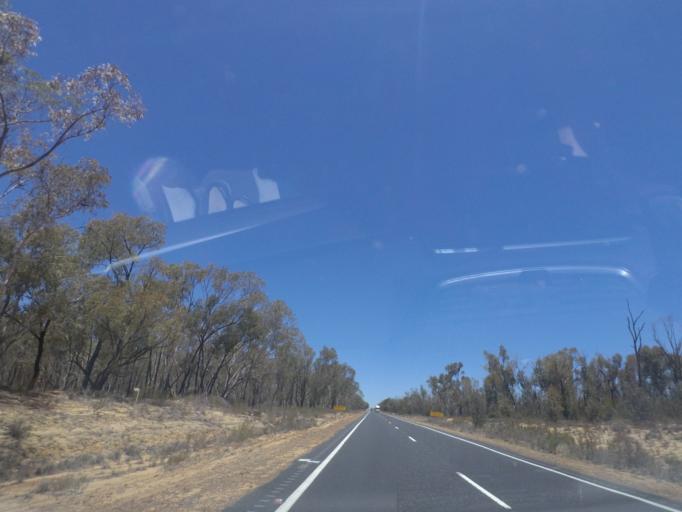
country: AU
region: New South Wales
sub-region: Warrumbungle Shire
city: Coonabarabran
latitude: -30.9539
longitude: 149.4209
